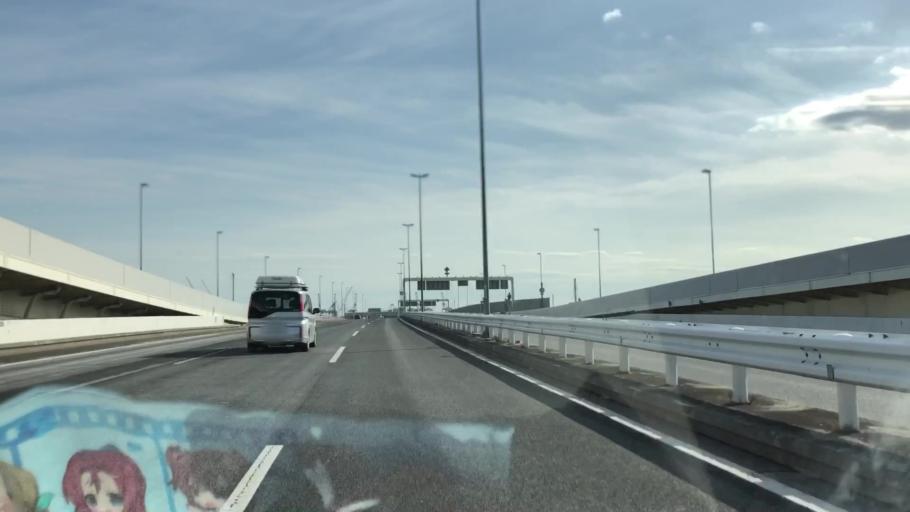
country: JP
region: Kanagawa
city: Yokohama
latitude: 35.4344
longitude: 139.6700
